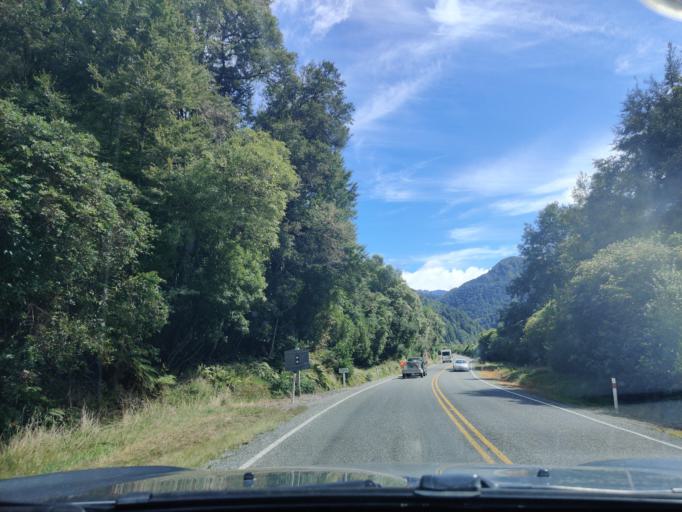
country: NZ
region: West Coast
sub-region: Buller District
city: Westport
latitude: -41.7787
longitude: 172.2477
